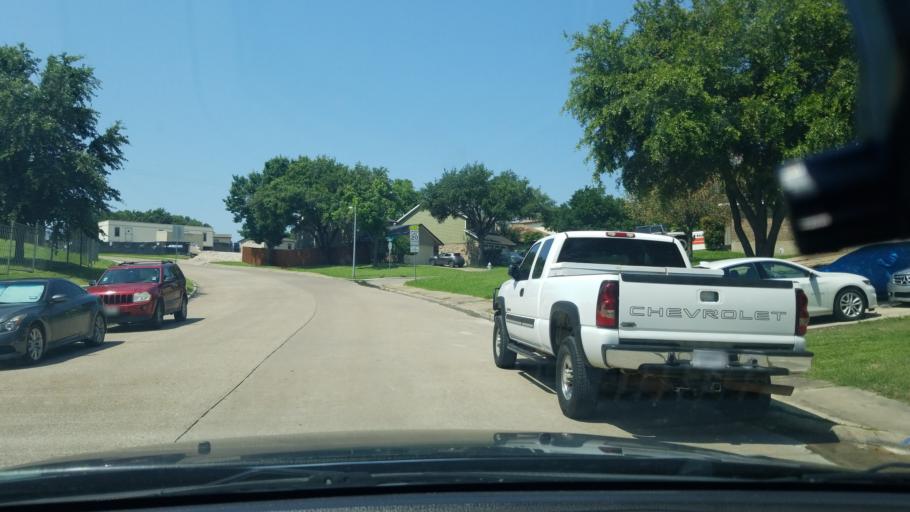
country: US
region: Texas
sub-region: Dallas County
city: Sunnyvale
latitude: 32.8295
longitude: -96.6022
